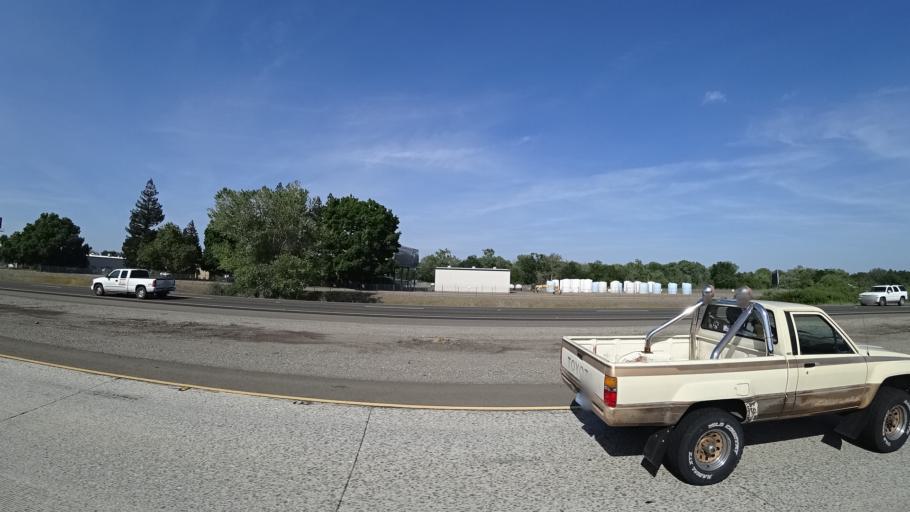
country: US
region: California
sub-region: Butte County
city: Durham
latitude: 39.6963
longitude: -121.7805
